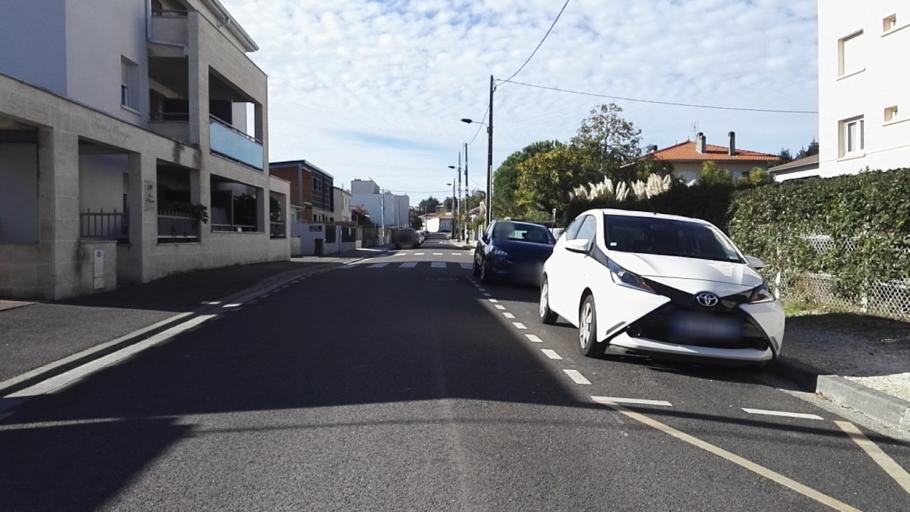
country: FR
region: Aquitaine
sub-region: Departement de la Gironde
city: Bruges
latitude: 44.8613
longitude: -0.6205
